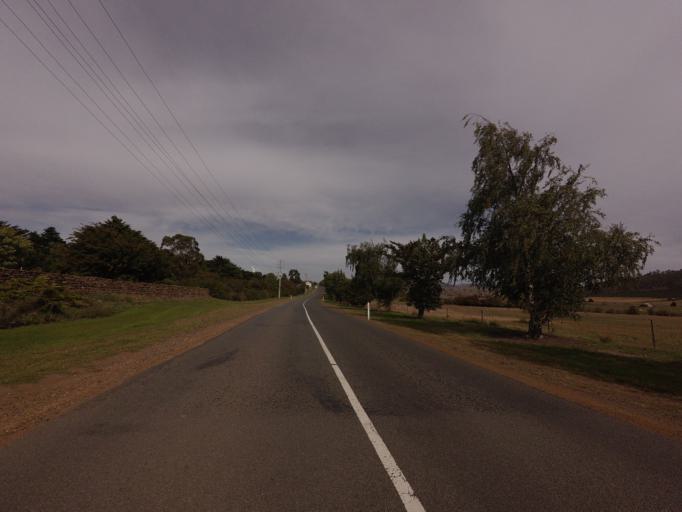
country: AU
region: Tasmania
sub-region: Brighton
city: Bridgewater
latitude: -42.2975
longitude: 147.3811
